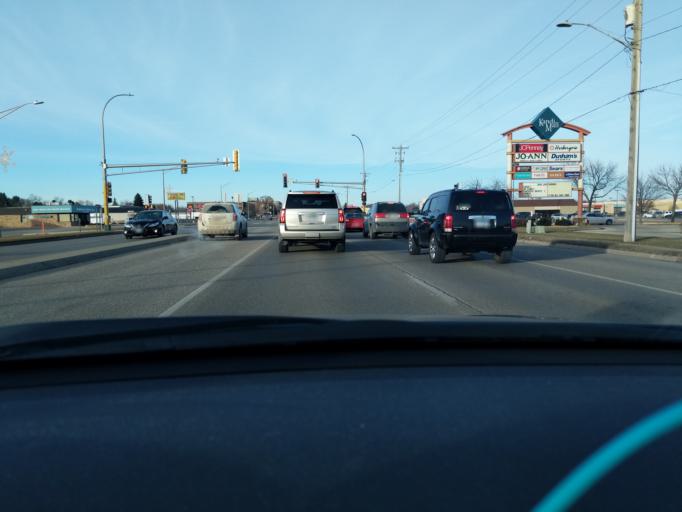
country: US
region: Minnesota
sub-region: Kandiyohi County
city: Willmar
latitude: 45.1052
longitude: -95.0426
